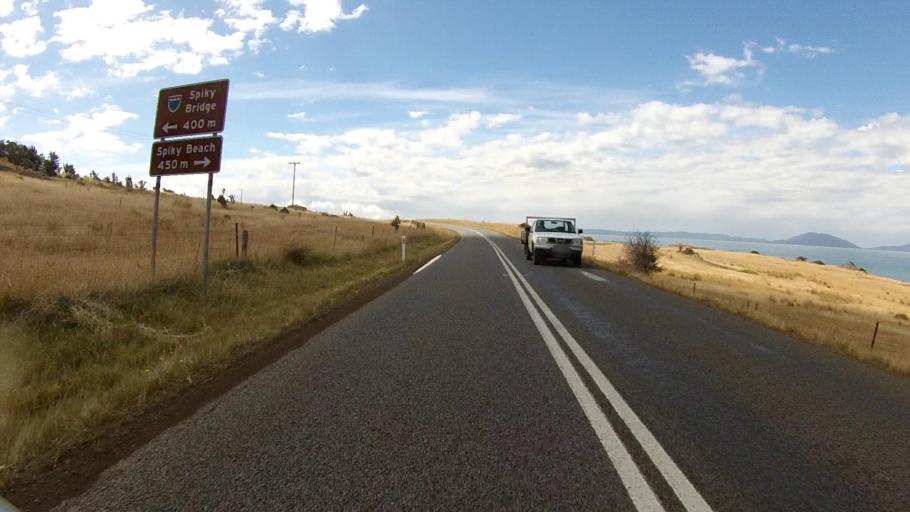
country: AU
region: Tasmania
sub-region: Sorell
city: Sorell
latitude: -42.1900
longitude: 148.0639
